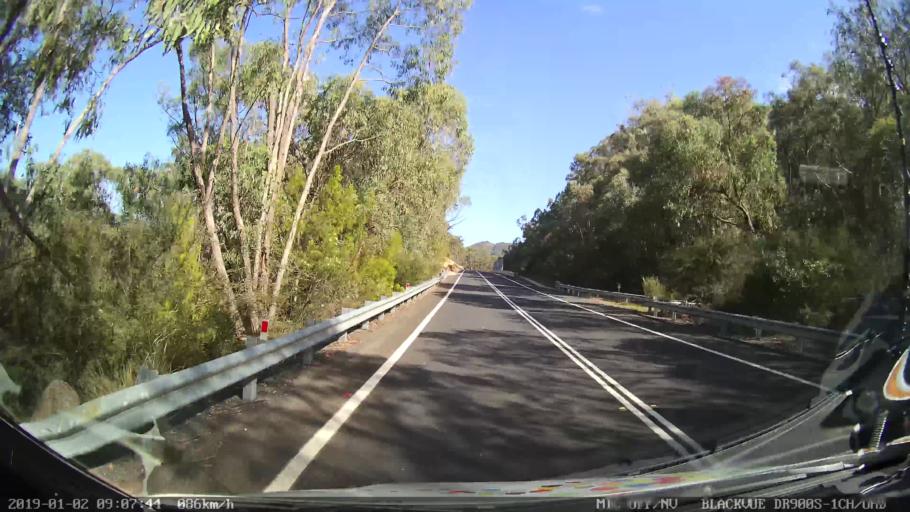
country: AU
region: New South Wales
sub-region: Tumut Shire
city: Tumut
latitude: -35.5376
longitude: 148.2965
